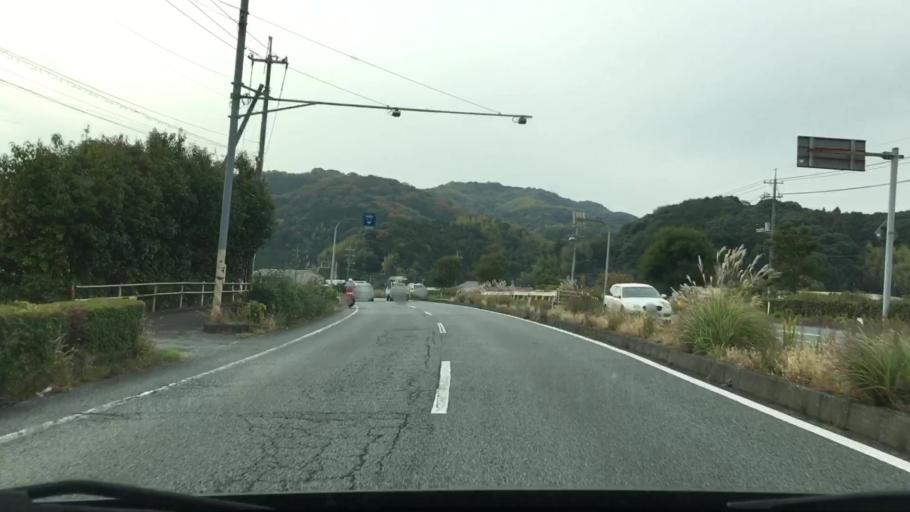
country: JP
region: Yamaguchi
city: Tokuyama
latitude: 34.0810
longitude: 131.7146
